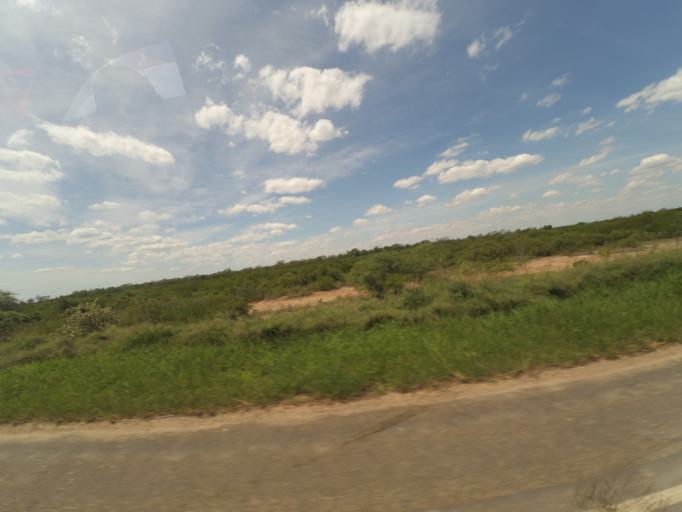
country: BO
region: Santa Cruz
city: Pailon
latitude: -17.5890
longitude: -61.9648
